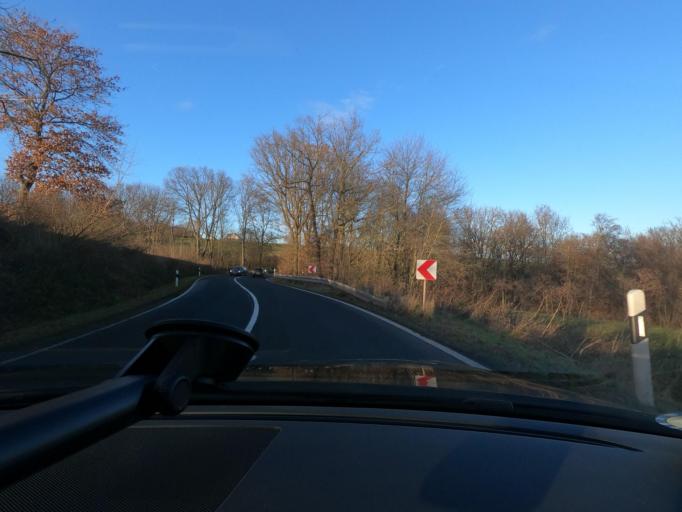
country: DE
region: Lower Saxony
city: Rhumspringe
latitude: 51.5408
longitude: 10.2937
